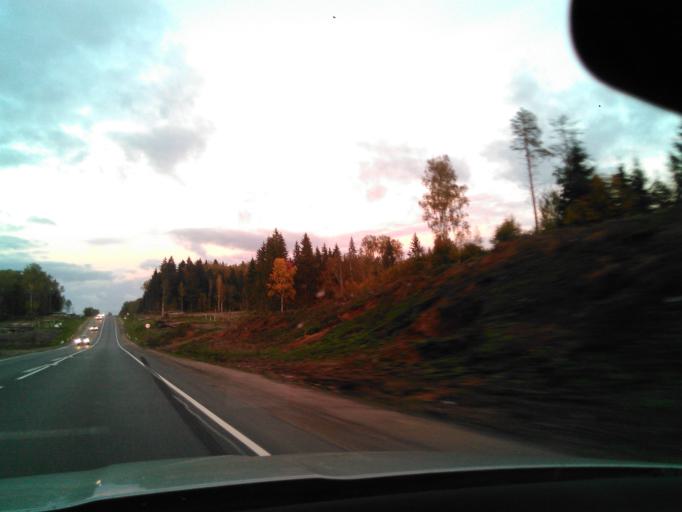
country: RU
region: Moskovskaya
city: Radumlya
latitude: 56.0466
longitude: 37.1114
